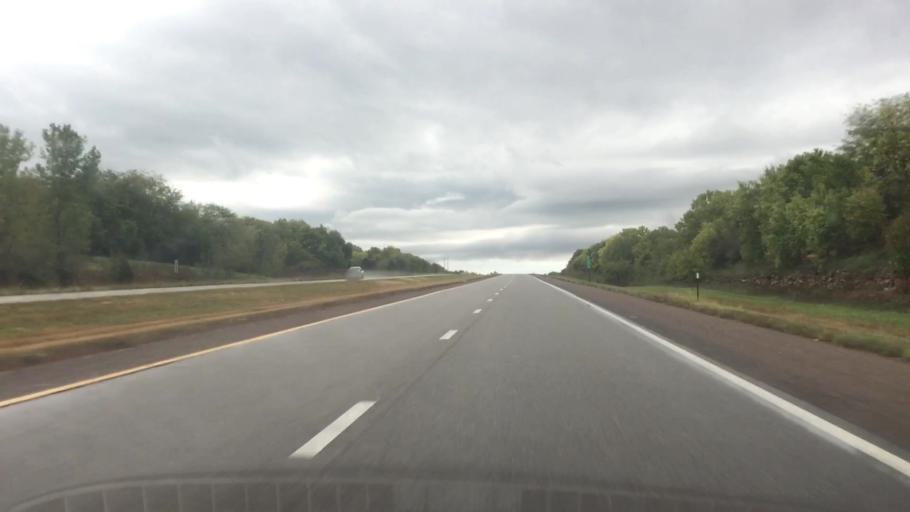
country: US
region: Kansas
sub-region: Miami County
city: Paola
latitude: 38.5951
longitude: -94.8356
